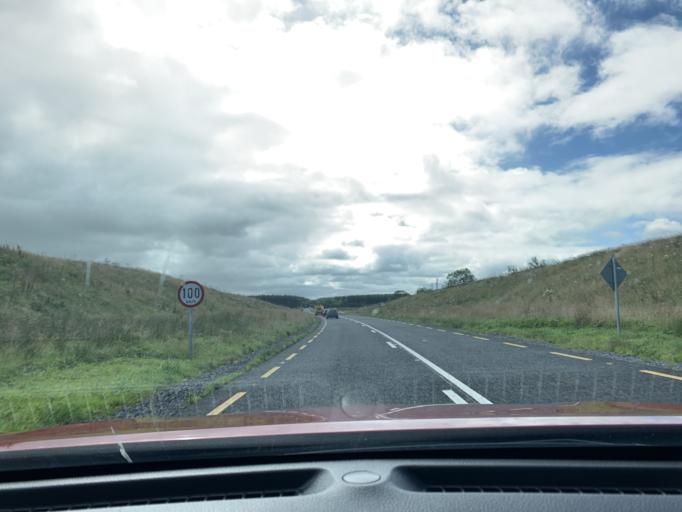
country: IE
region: Connaught
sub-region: Roscommon
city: Boyle
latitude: 53.9227
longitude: -8.2765
